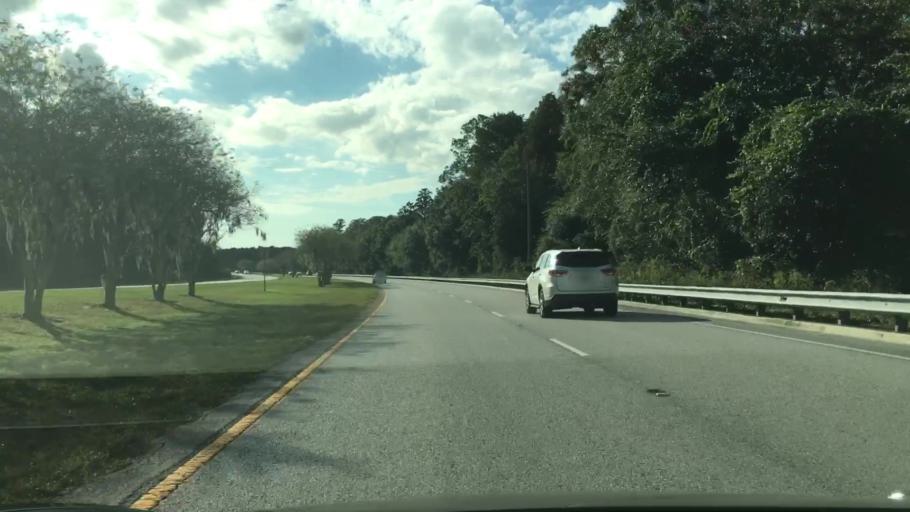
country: US
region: Florida
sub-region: Pasco County
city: Trinity
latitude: 28.1707
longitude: -82.6820
